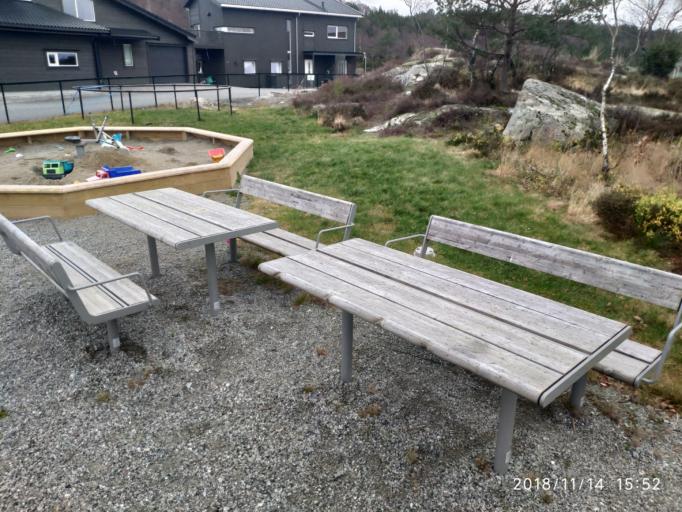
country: NO
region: Rogaland
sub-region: Strand
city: Tau
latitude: 59.0701
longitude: 5.9138
